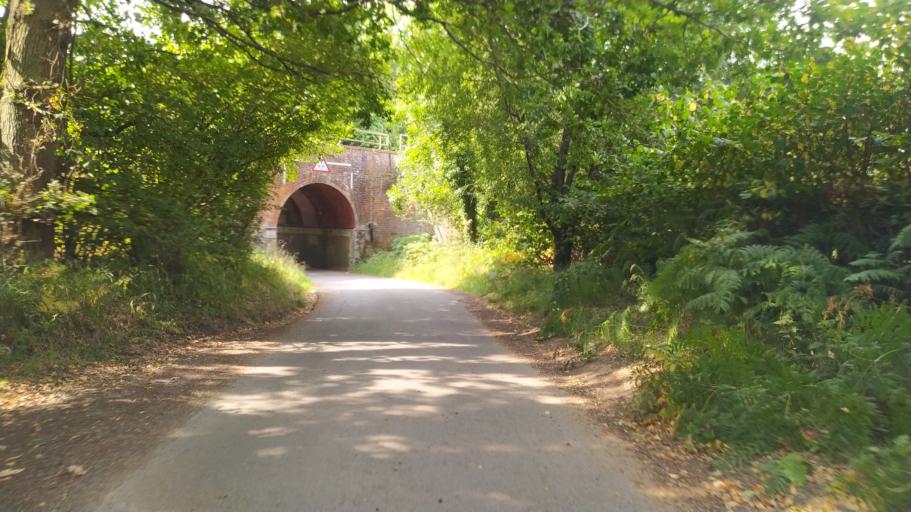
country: GB
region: England
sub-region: Hampshire
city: Romsey
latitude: 50.9975
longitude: -1.4440
